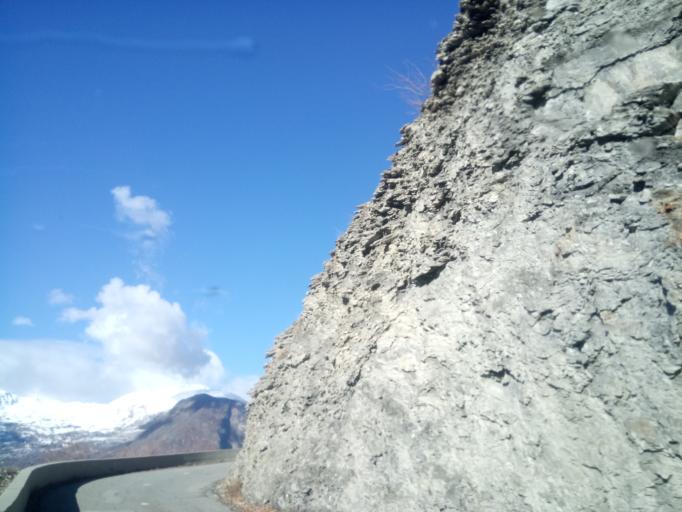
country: FR
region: Rhone-Alpes
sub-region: Departement de la Savoie
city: Villargondran
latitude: 45.2700
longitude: 6.3845
